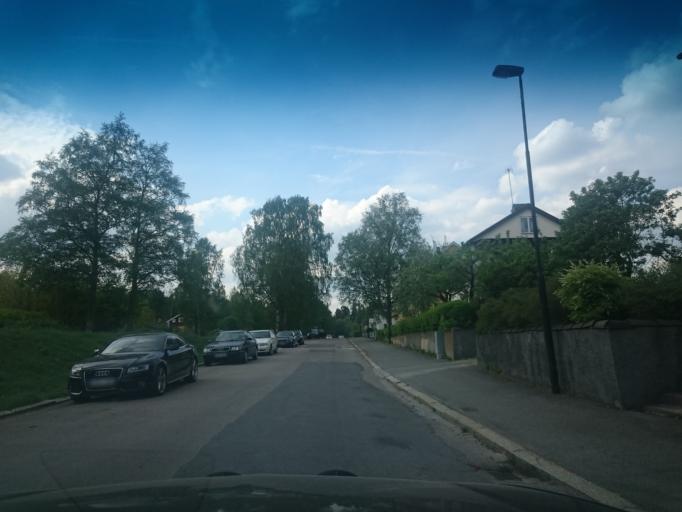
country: SE
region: Joenkoeping
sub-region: Vetlanda Kommun
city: Vetlanda
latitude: 57.4305
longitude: 15.0712
